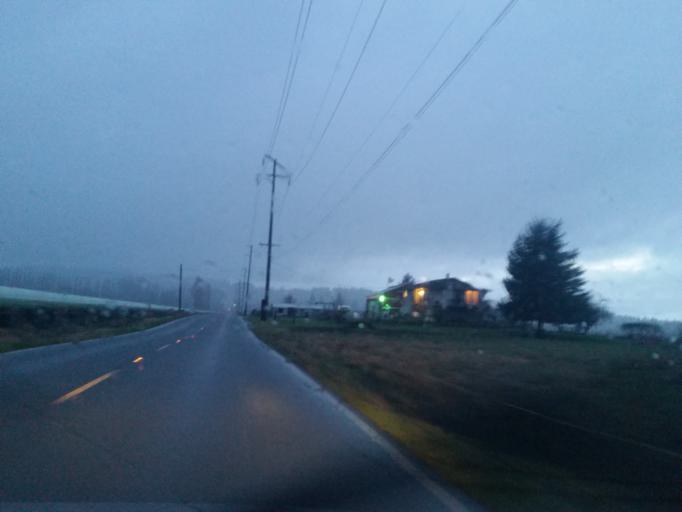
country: US
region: Washington
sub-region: Snohomish County
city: Fobes Hill
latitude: 47.9494
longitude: -122.1646
